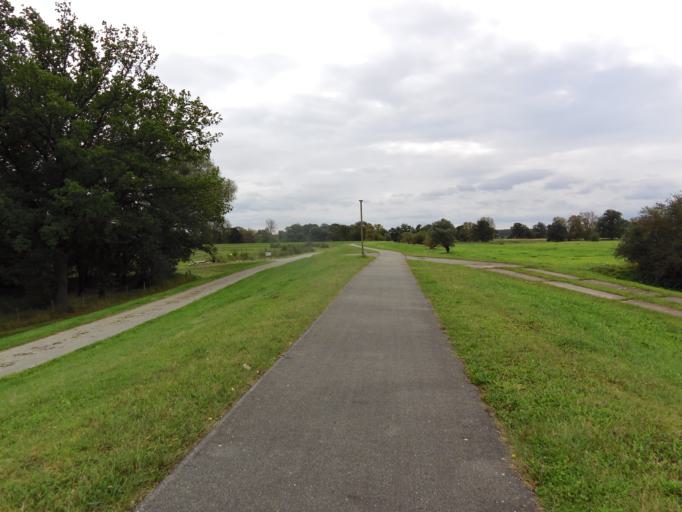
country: DE
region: Brandenburg
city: Ruhstadt
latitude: 52.9172
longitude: 11.8428
